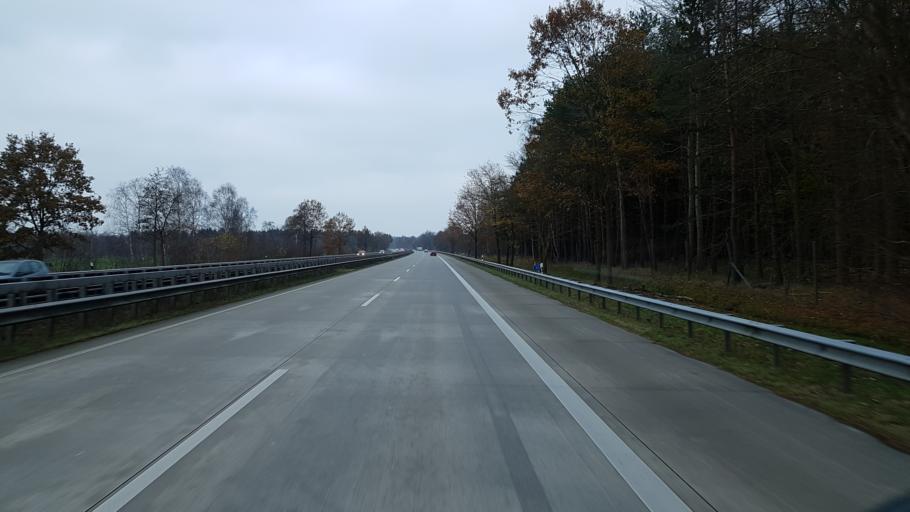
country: DE
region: Lower Saxony
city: Schwanewede
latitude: 53.2633
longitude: 8.6360
